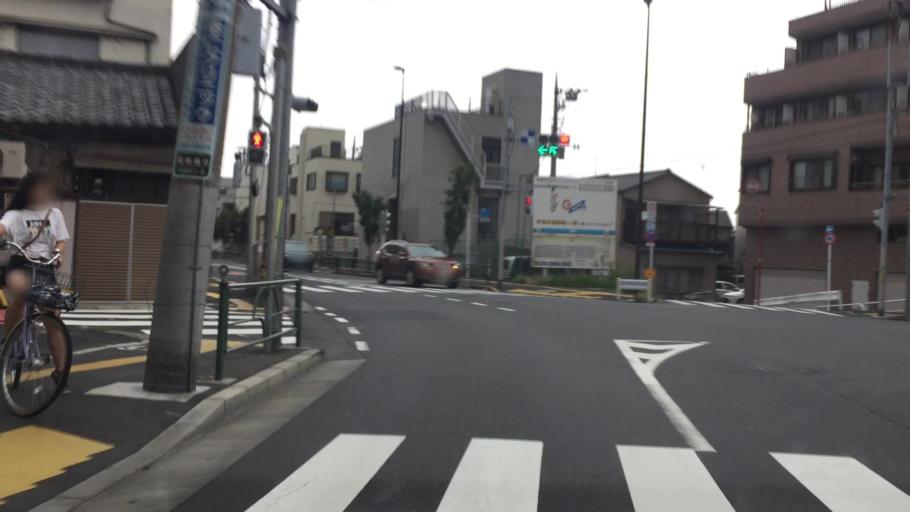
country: JP
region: Saitama
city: Soka
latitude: 35.7506
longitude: 139.7944
